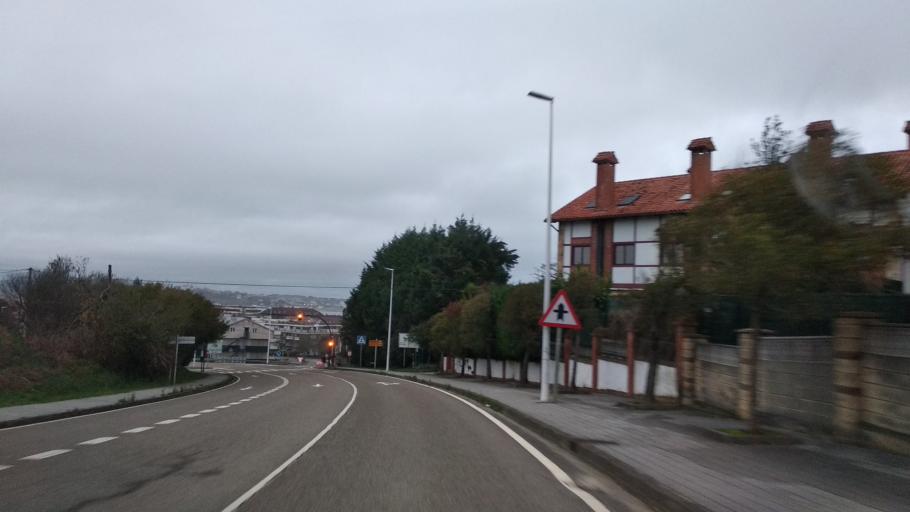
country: ES
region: Cantabria
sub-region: Provincia de Cantabria
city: Santander
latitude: 43.4528
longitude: -3.7398
